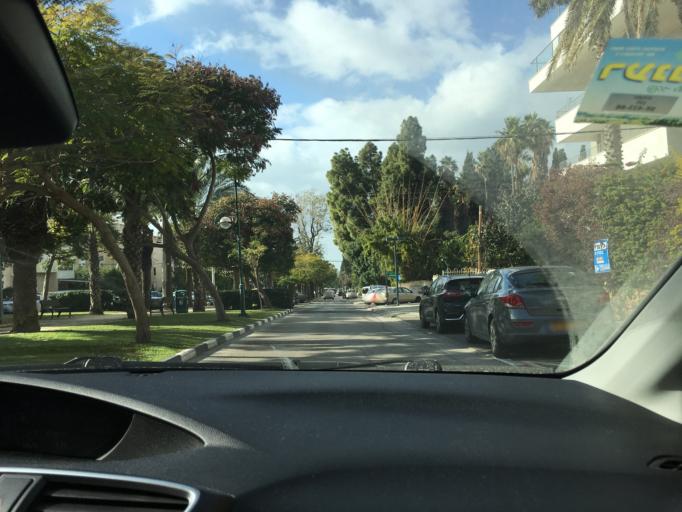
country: IL
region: Tel Aviv
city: Ramat HaSharon
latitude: 32.1450
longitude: 34.8419
